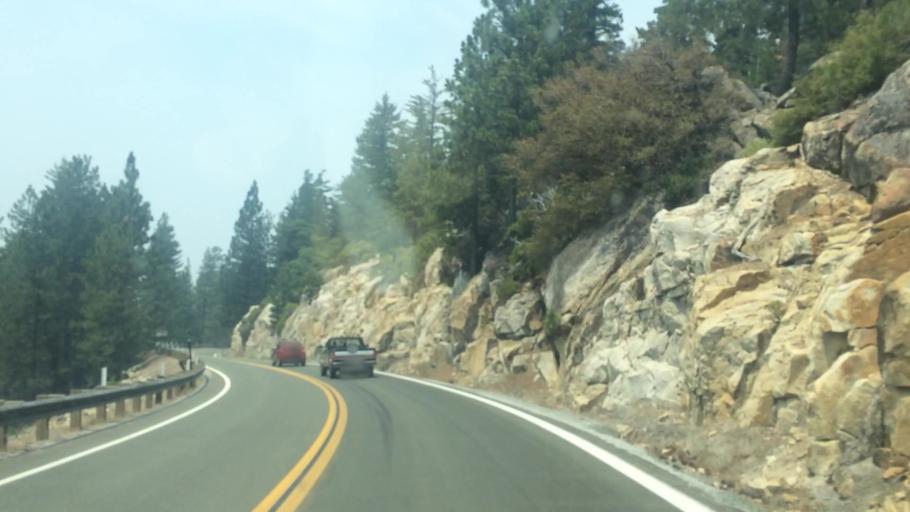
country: US
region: California
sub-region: Amador County
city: Pioneer
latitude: 38.5432
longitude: -120.3482
